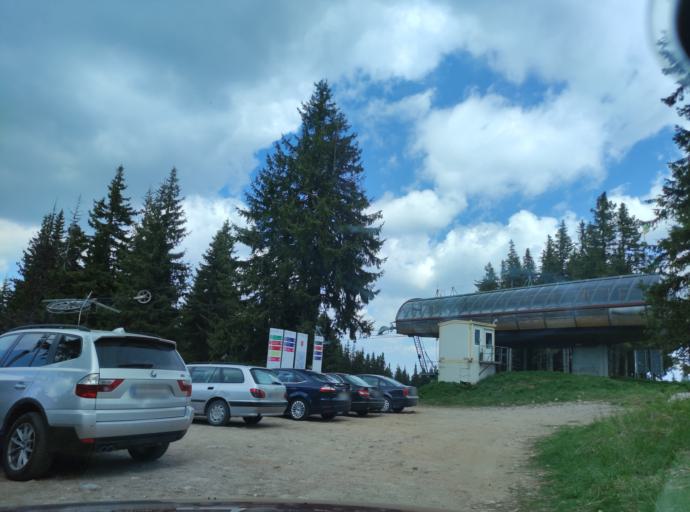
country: BG
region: Smolyan
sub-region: Obshtina Smolyan
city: Smolyan
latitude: 41.6369
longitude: 24.6782
